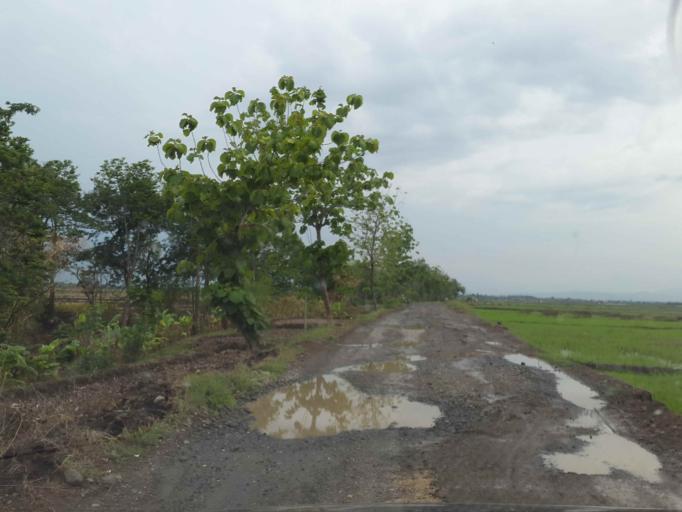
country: ID
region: Central Java
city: Ketanggungan
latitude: -6.9478
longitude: 108.9451
